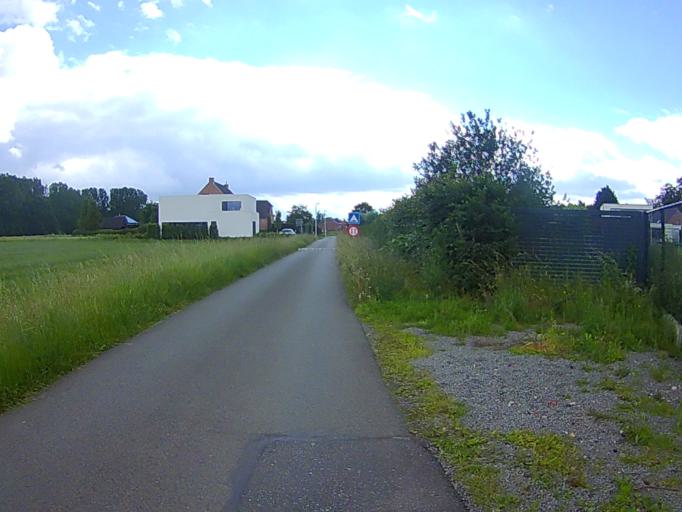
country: BE
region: Flanders
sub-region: Provincie Antwerpen
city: Lier
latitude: 51.1592
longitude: 4.5801
